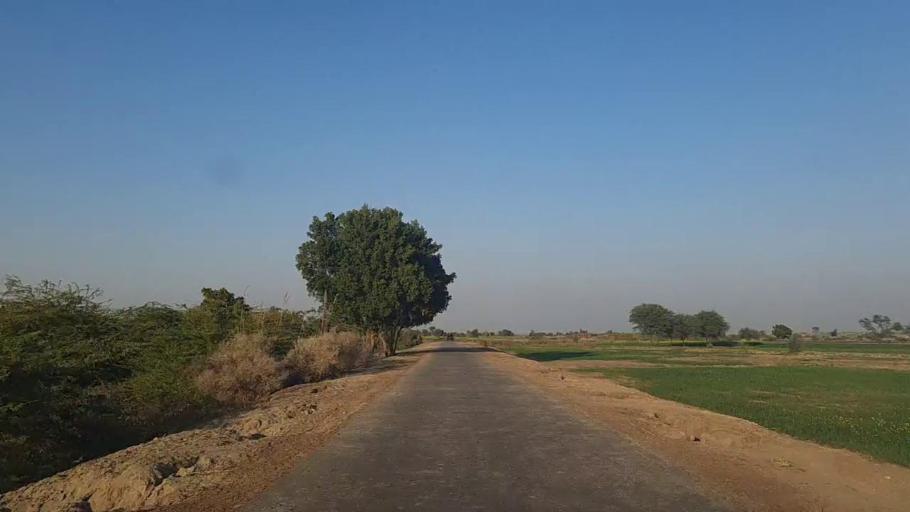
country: PK
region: Sindh
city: Jam Sahib
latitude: 26.3416
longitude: 68.6711
